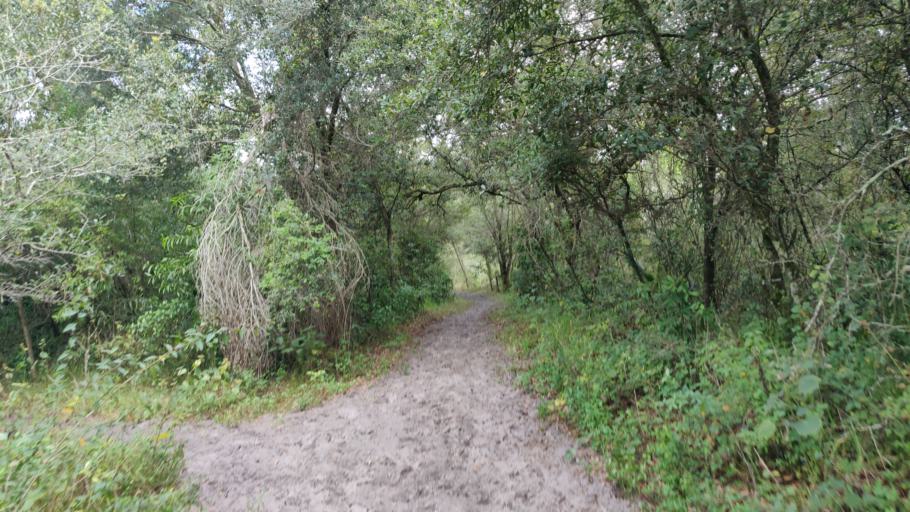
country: US
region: Florida
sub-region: Broward County
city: Cooper City
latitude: 26.0744
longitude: -80.2713
